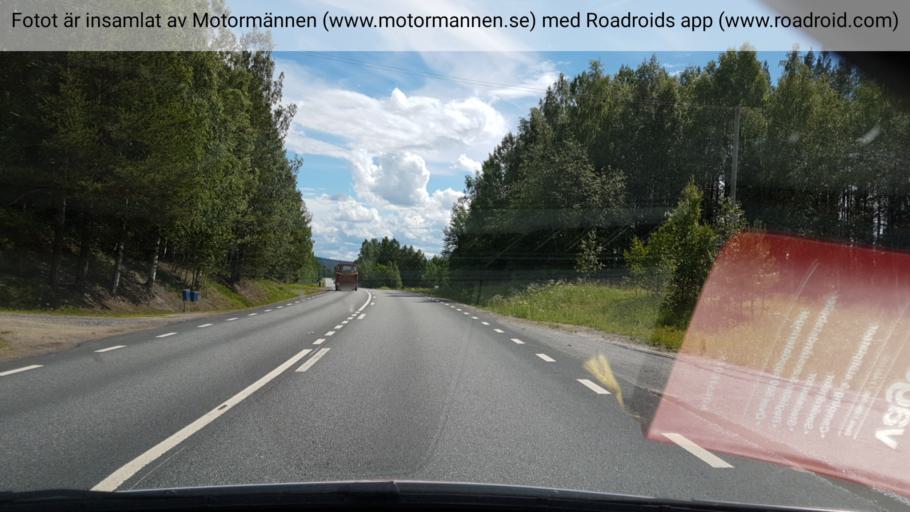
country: SE
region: Vaesternorrland
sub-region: Solleftea Kommun
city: Solleftea
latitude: 63.2694
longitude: 17.2088
